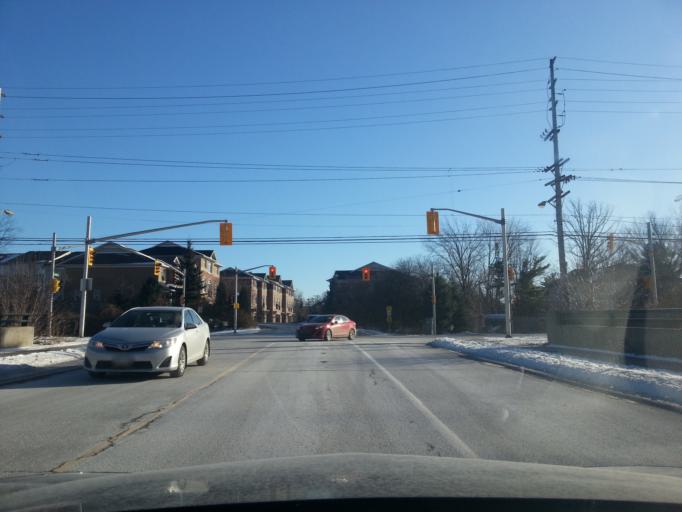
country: CA
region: Ontario
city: Ottawa
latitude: 45.3980
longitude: -75.7490
